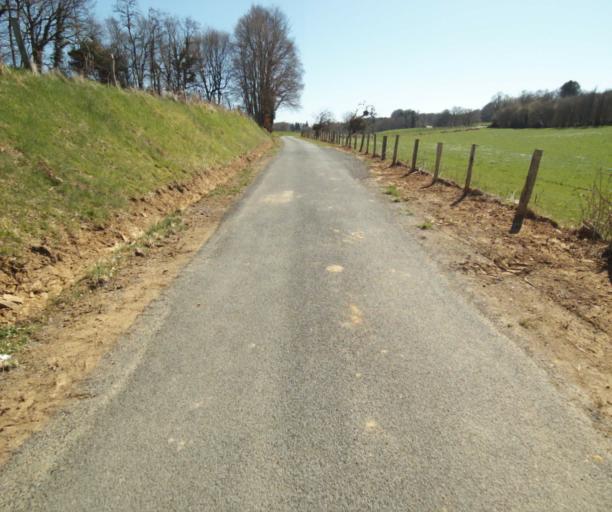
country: FR
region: Limousin
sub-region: Departement de la Correze
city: Uzerche
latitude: 45.3972
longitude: 1.6084
